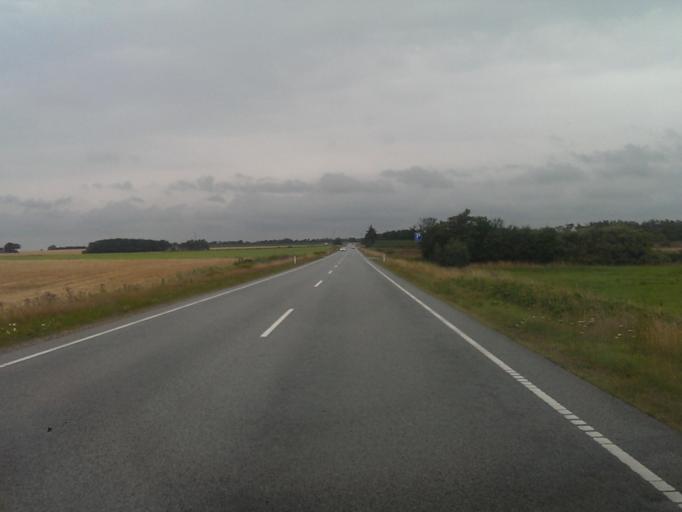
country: DK
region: South Denmark
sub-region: Esbjerg Kommune
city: Bramming
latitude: 55.5555
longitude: 8.6411
